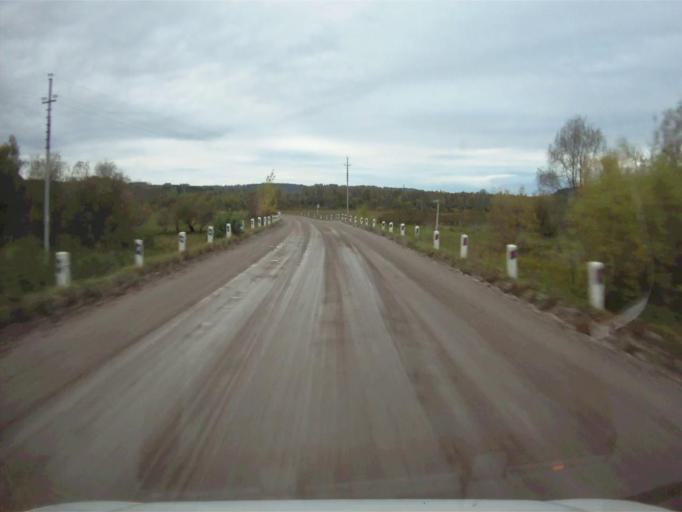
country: RU
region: Chelyabinsk
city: Nyazepetrovsk
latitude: 56.1251
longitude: 59.3535
